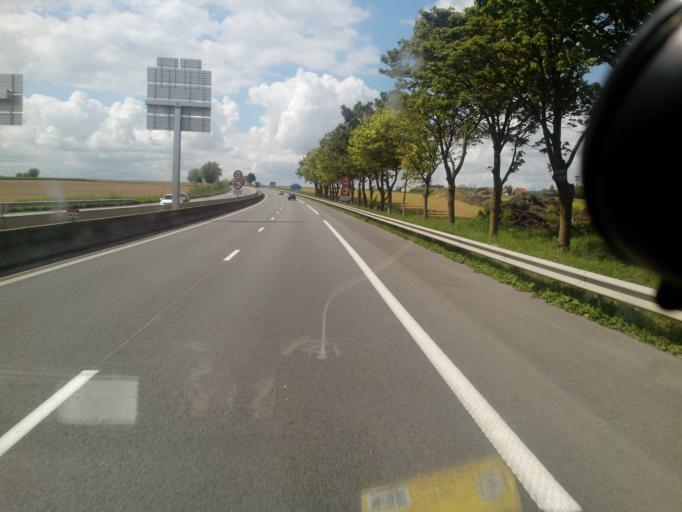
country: FR
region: Nord-Pas-de-Calais
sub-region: Departement du Nord
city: Meteren
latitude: 50.7482
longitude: 2.6707
